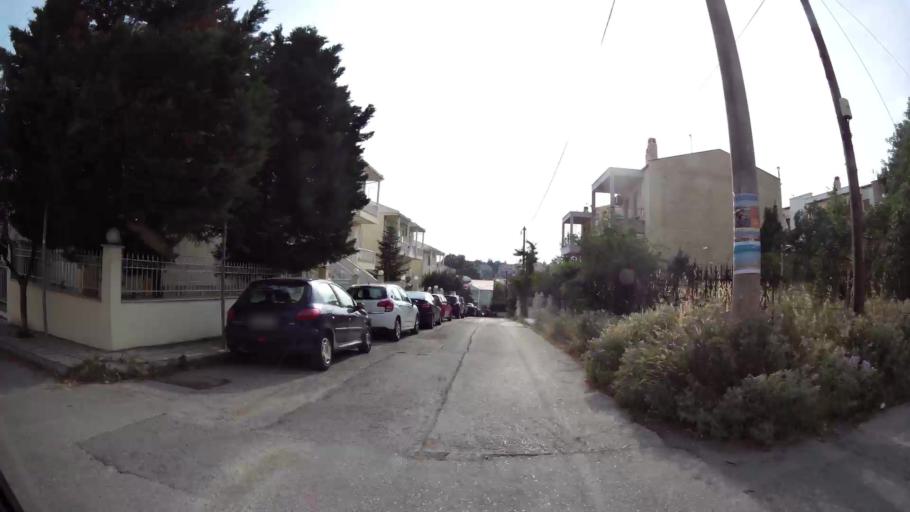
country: GR
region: Central Macedonia
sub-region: Nomos Thessalonikis
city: Oraiokastro
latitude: 40.7247
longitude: 22.9228
